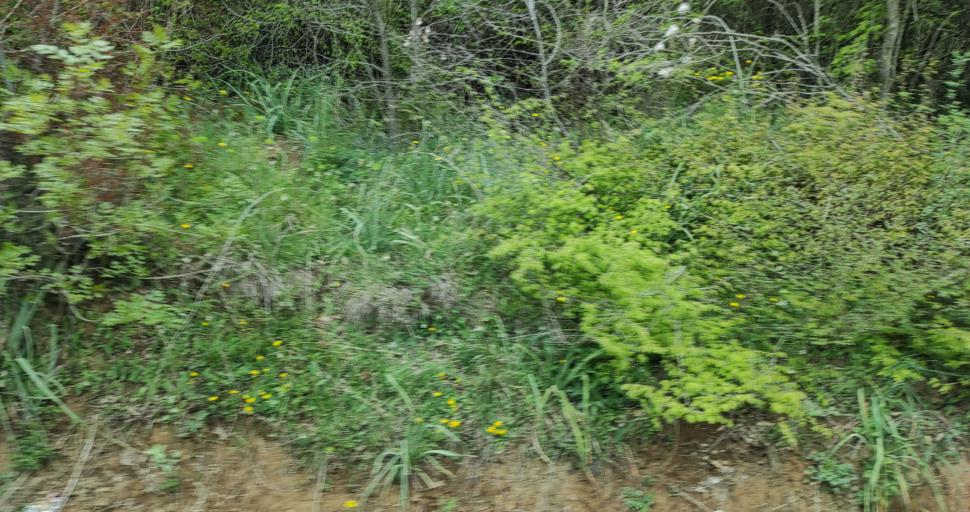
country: AL
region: Shkoder
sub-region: Rrethi i Shkodres
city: Dajc
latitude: 42.0260
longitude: 19.4215
